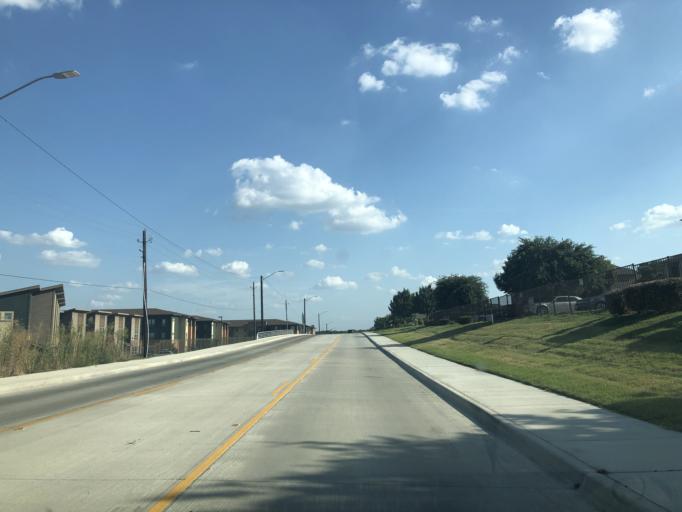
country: US
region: Texas
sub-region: Tarrant County
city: Sansom Park
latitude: 32.8216
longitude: -97.3795
